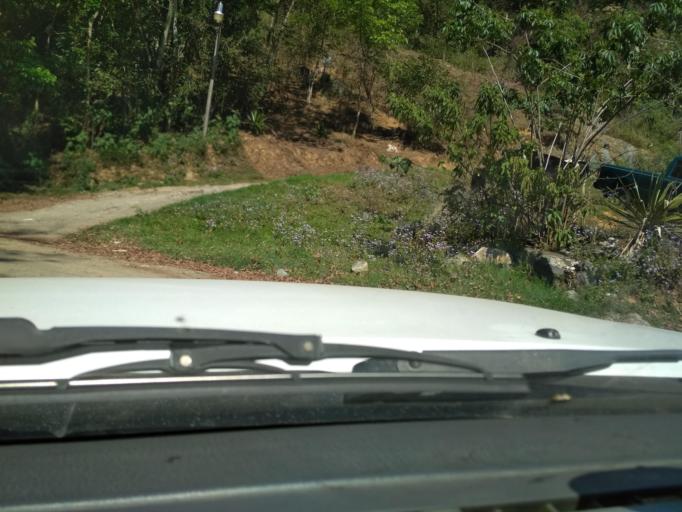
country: MX
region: Veracruz
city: Tequila
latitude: 18.7511
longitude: -97.0913
